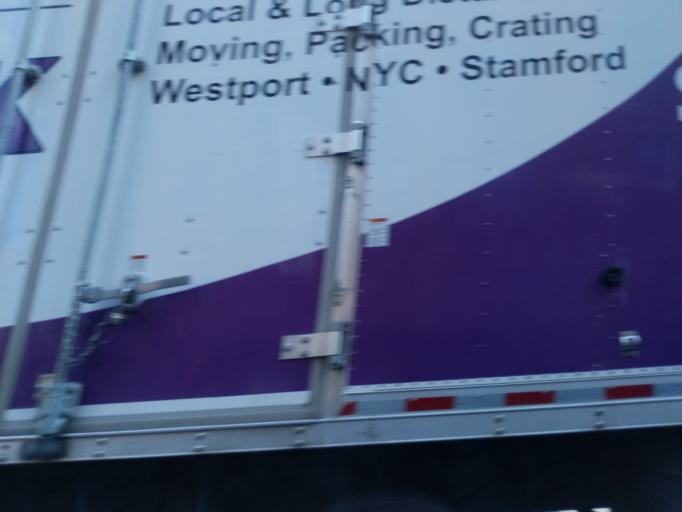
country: US
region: New York
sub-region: New York County
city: Manhattan
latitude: 40.8075
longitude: -73.9134
